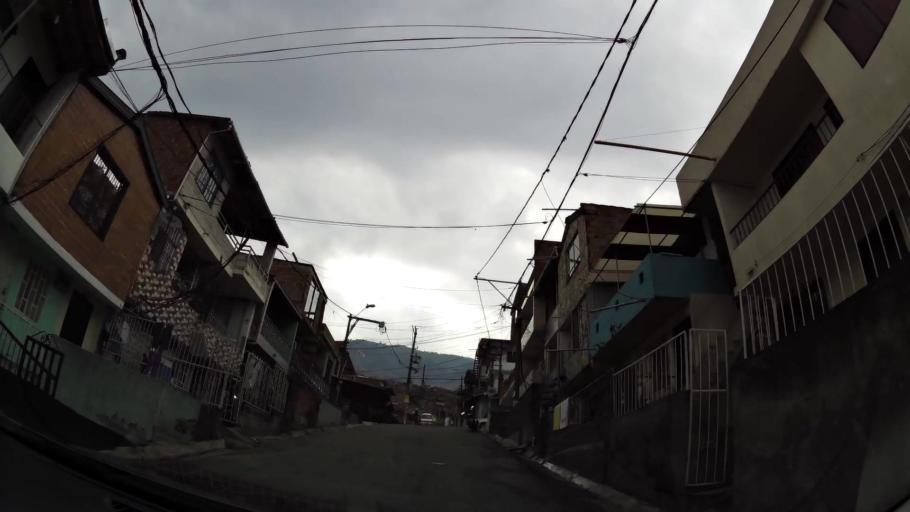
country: CO
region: Antioquia
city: Medellin
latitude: 6.2940
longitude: -75.5569
